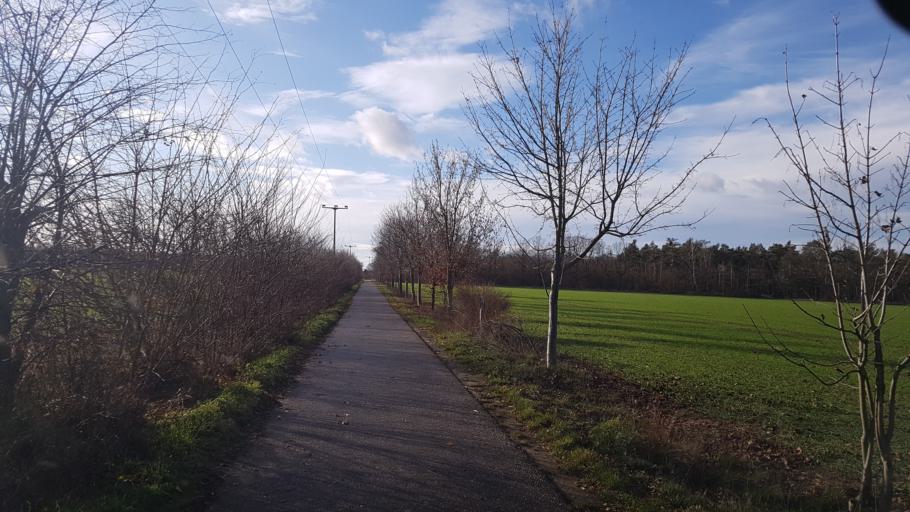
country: DE
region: Brandenburg
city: Falkenberg
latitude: 51.5989
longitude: 13.2787
